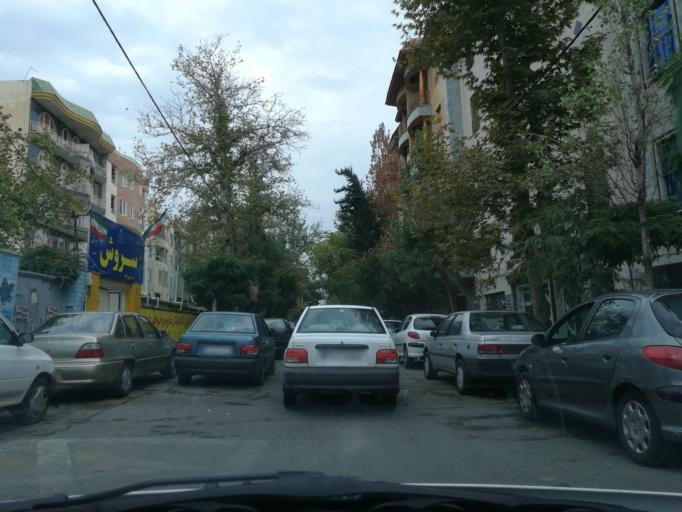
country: IR
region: Alborz
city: Karaj
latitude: 35.8551
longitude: 50.9530
